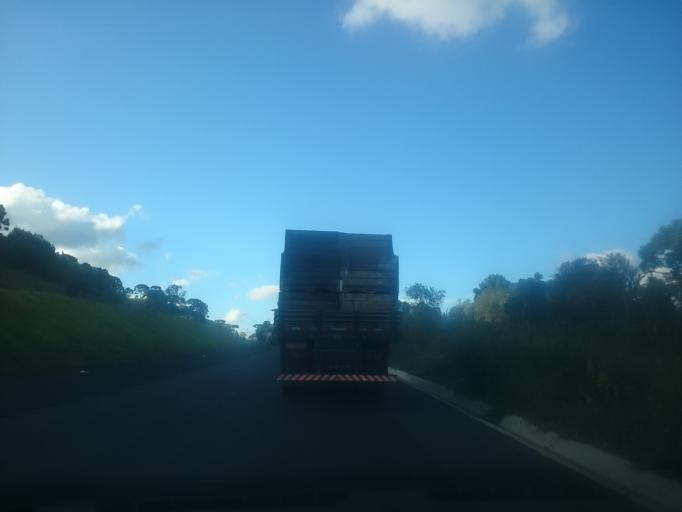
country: BR
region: Santa Catarina
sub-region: Sao Joaquim
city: Sao Joaquim
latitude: -28.0651
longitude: -50.0732
